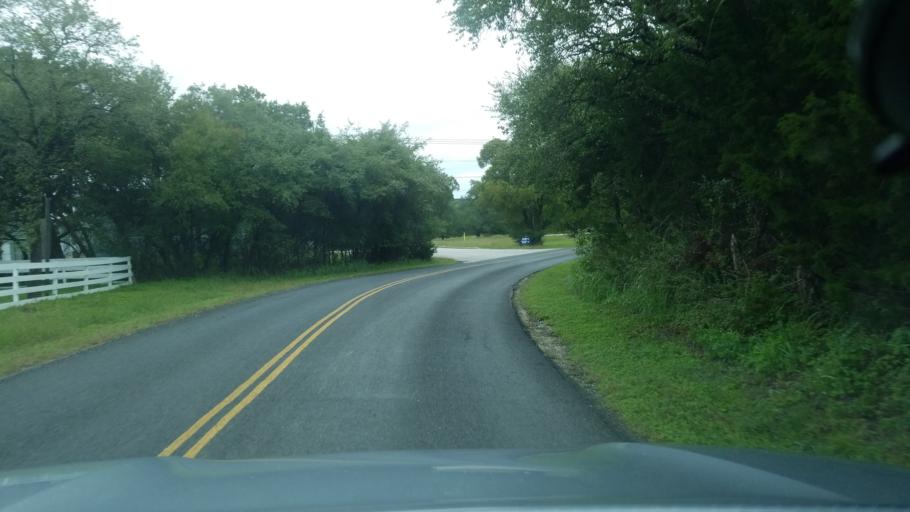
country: US
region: Texas
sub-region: Comal County
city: Bulverde
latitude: 29.7952
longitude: -98.4256
